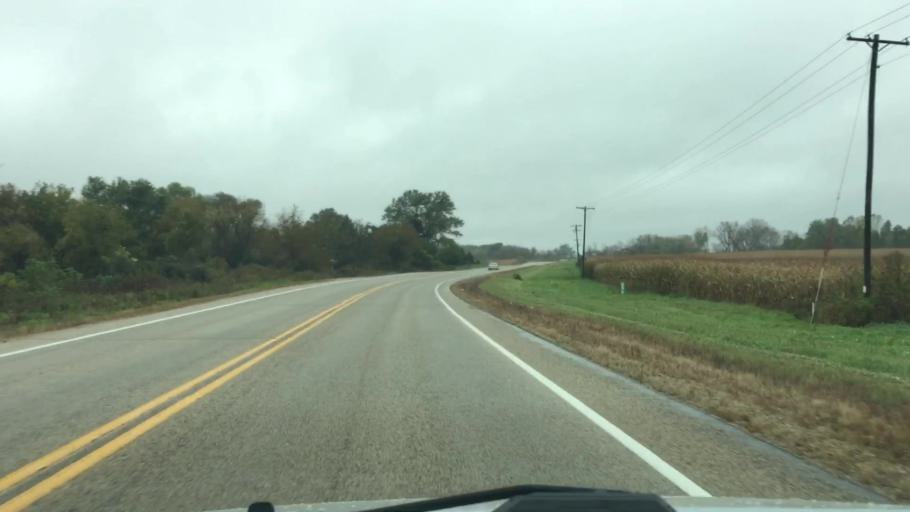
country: US
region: Wisconsin
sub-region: Jefferson County
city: Palmyra
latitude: 42.8787
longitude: -88.6100
